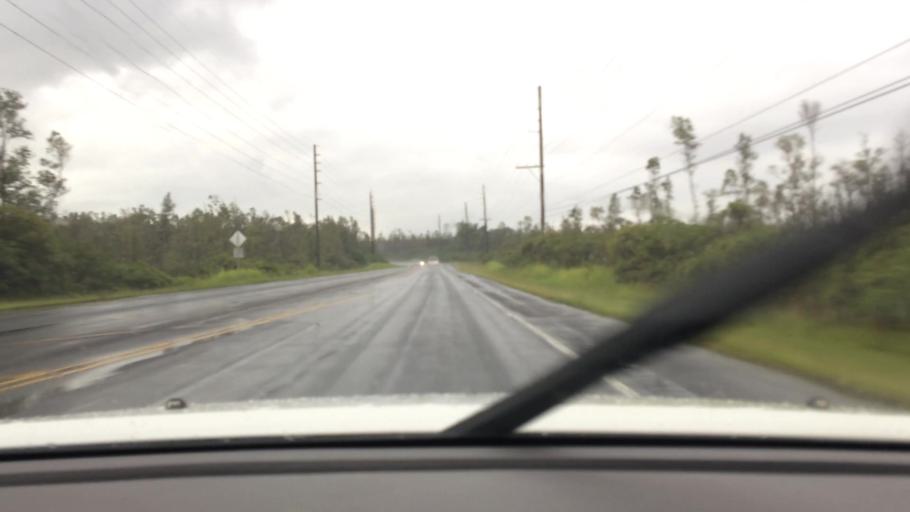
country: US
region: Hawaii
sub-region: Hawaii County
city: Ainaloa
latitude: 19.5296
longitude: -154.9711
